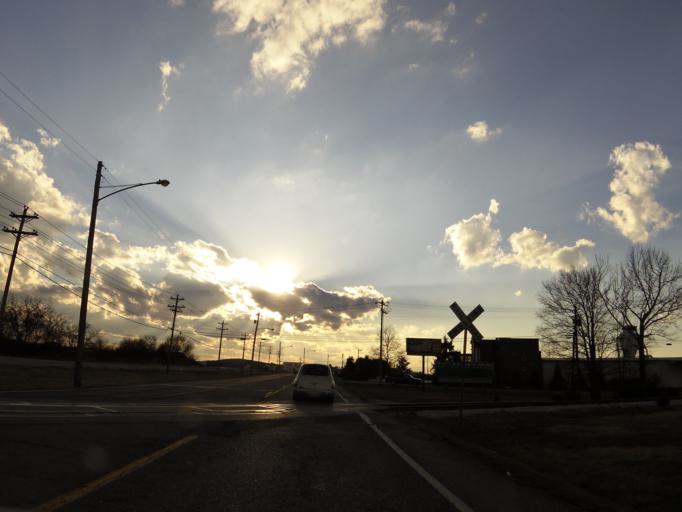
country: US
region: Tennessee
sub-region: Wilson County
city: Lebanon
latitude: 36.2188
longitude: -86.3226
